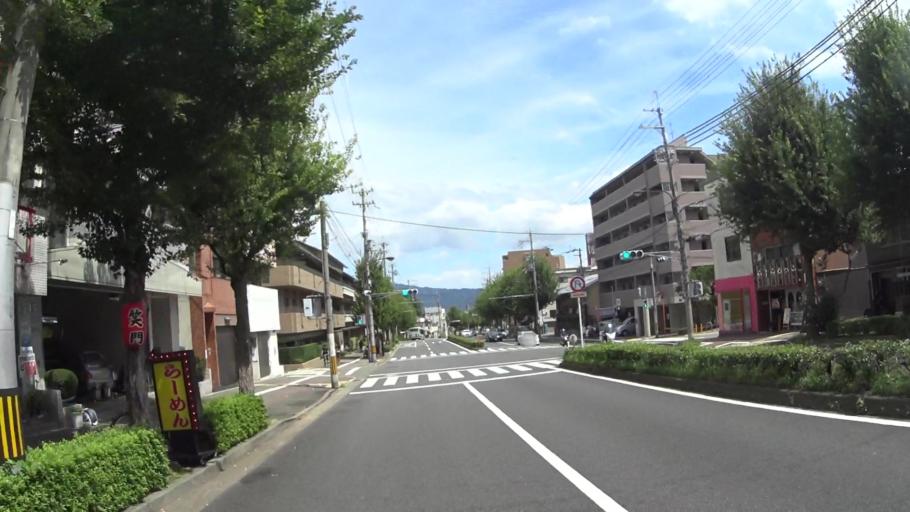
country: JP
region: Kyoto
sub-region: Kyoto-shi
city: Kamigyo-ku
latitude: 35.0411
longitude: 135.7404
